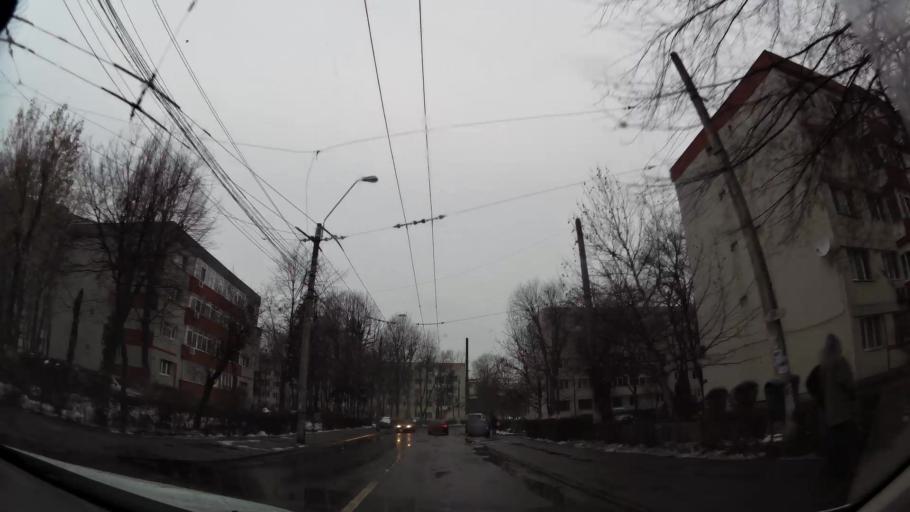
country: RO
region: Ilfov
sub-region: Comuna Chiajna
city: Rosu
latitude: 44.4828
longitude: 26.0553
